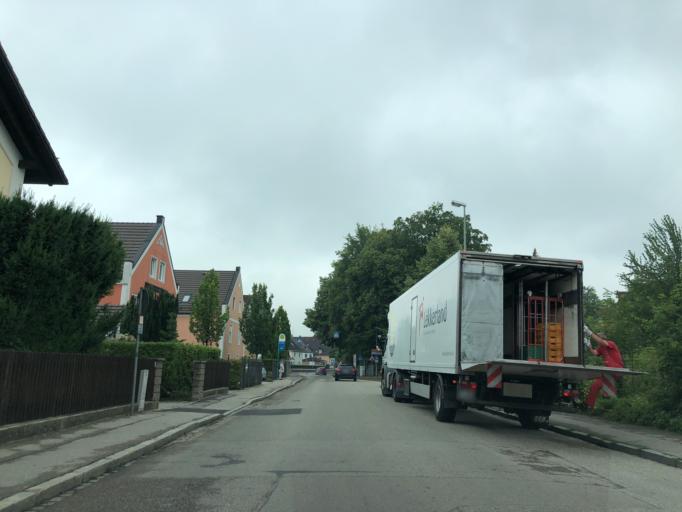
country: DE
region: Bavaria
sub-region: Upper Bavaria
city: Erding
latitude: 48.3019
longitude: 11.9081
